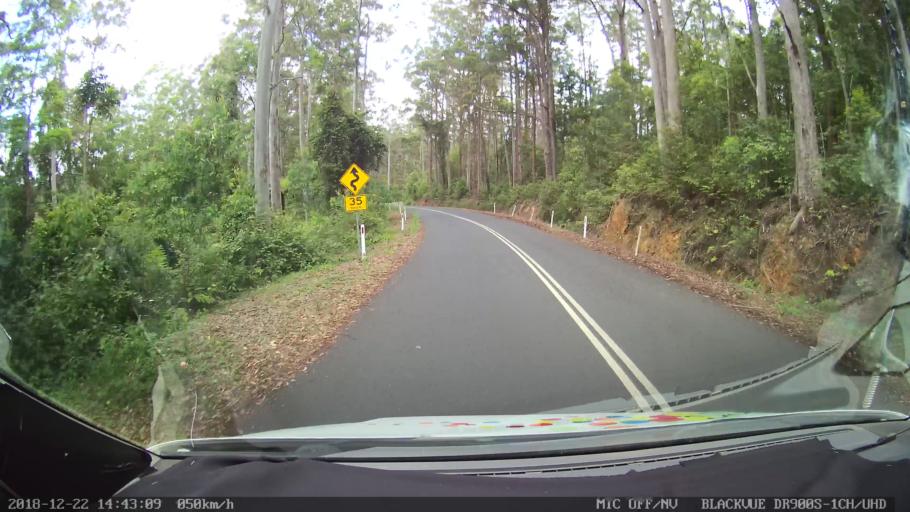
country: AU
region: New South Wales
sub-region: Bellingen
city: Dorrigo
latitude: -30.1646
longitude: 152.5855
